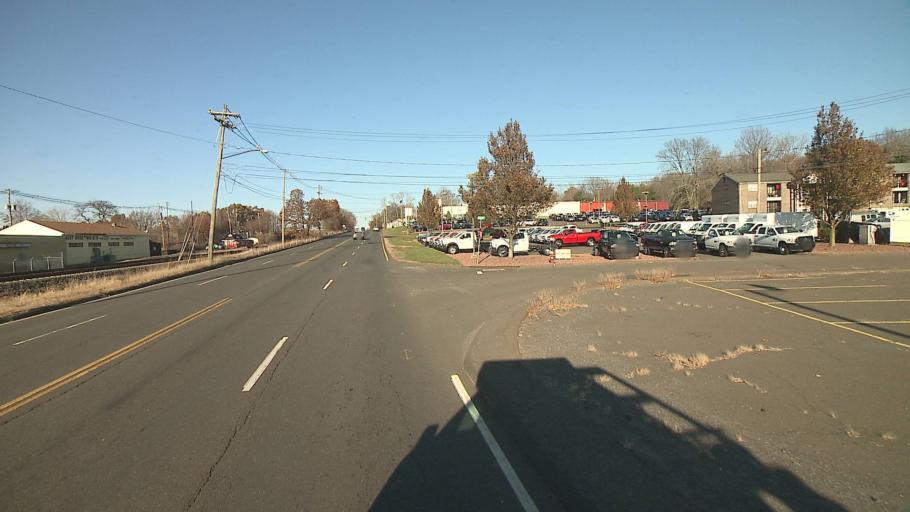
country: US
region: Connecticut
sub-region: New Haven County
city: Wallingford Center
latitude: 41.4433
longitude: -72.8308
